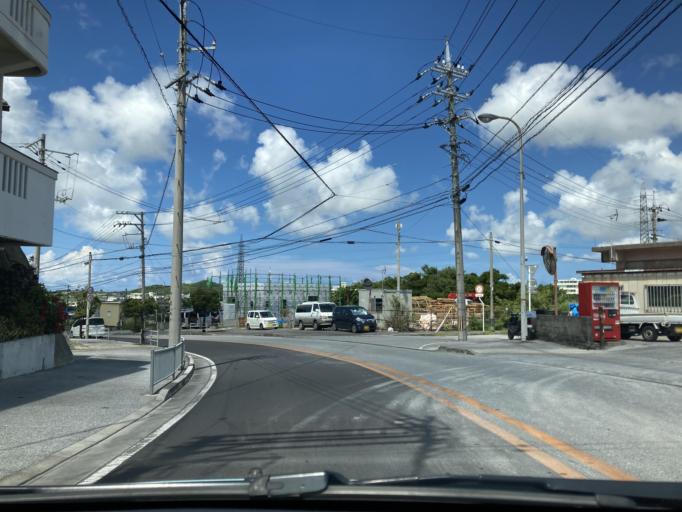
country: JP
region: Okinawa
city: Tomigusuku
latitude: 26.1654
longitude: 127.7224
